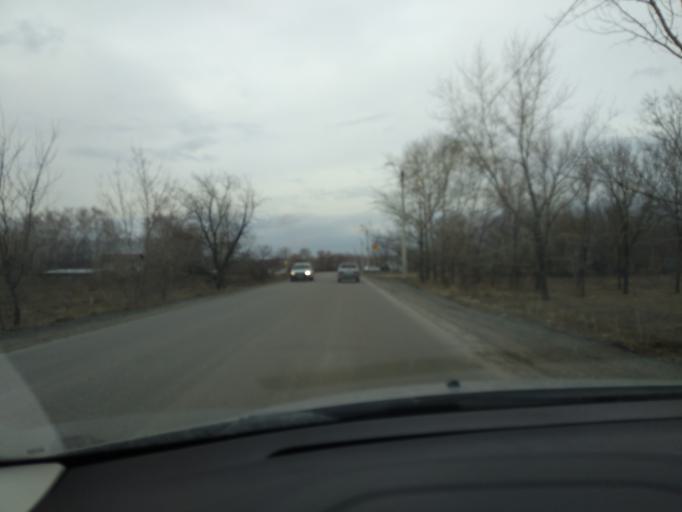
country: RU
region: Chelyabinsk
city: Potanino
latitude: 55.2863
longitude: 61.5136
